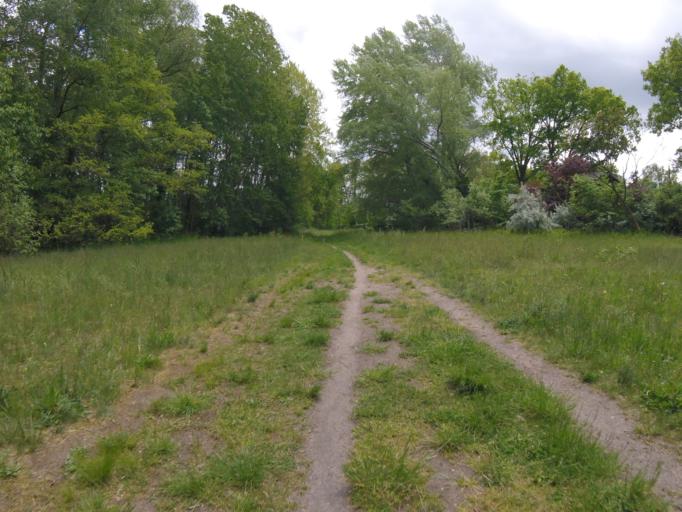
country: DE
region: Brandenburg
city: Bestensee
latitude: 52.2593
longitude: 13.6642
